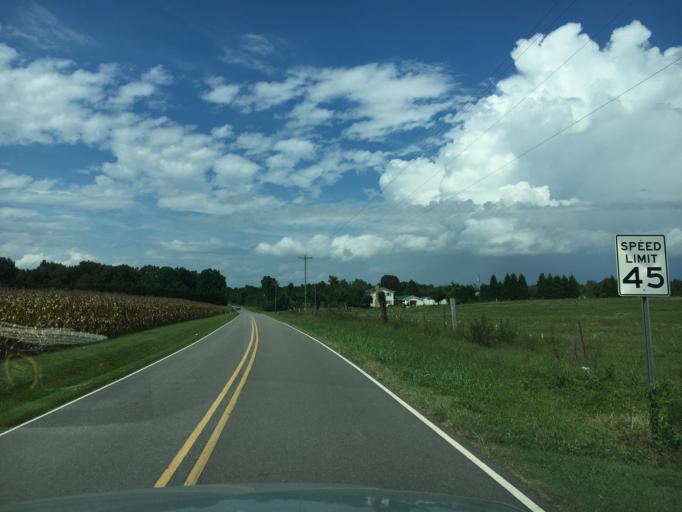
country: US
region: North Carolina
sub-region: Catawba County
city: Claremont
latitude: 35.6525
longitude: -81.1132
